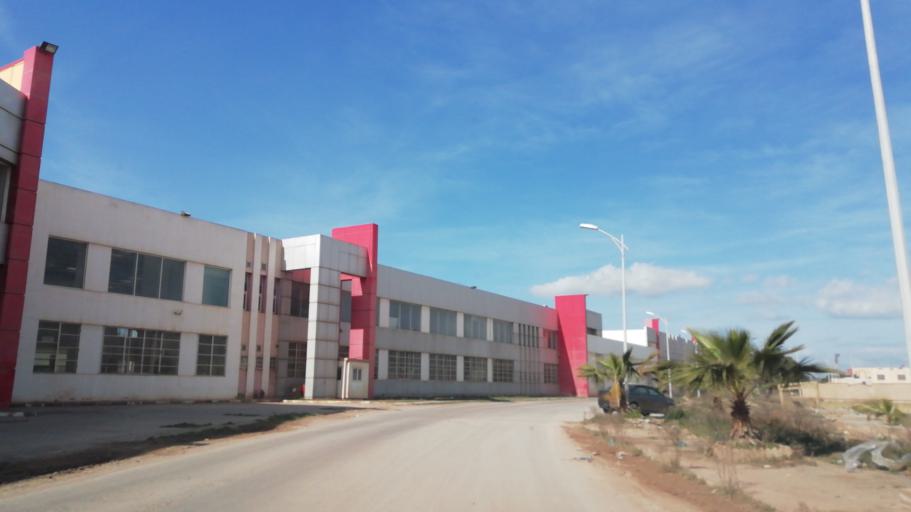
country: DZ
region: Oran
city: Es Senia
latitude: 35.6374
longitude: -0.5870
